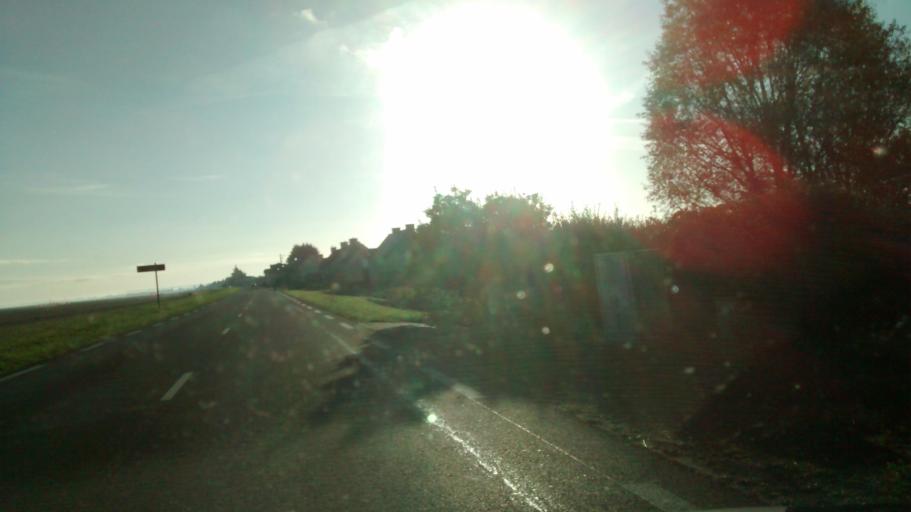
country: FR
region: Brittany
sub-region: Departement d'Ille-et-Vilaine
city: Hirel
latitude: 48.6090
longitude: -1.8181
